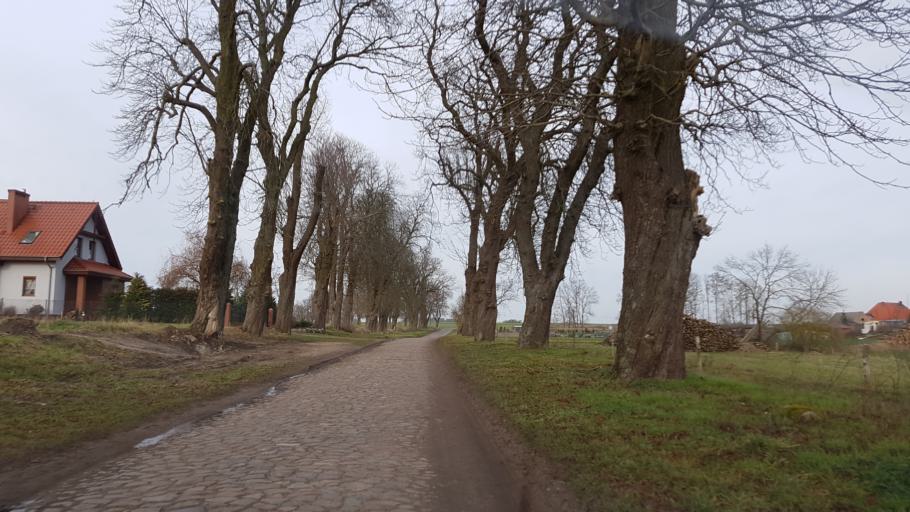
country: PL
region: Lubusz
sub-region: Powiat strzelecko-drezdenecki
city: Strzelce Krajenskie
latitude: 52.9293
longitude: 15.4175
